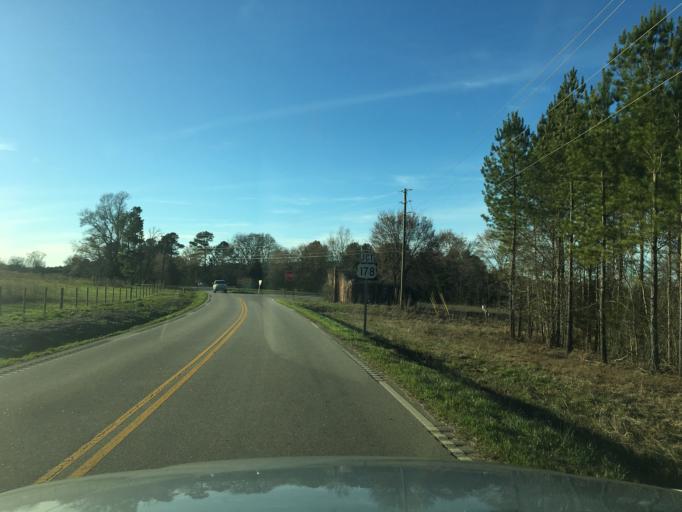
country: US
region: South Carolina
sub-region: Saluda County
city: Saluda
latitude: 33.9915
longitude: -81.7456
